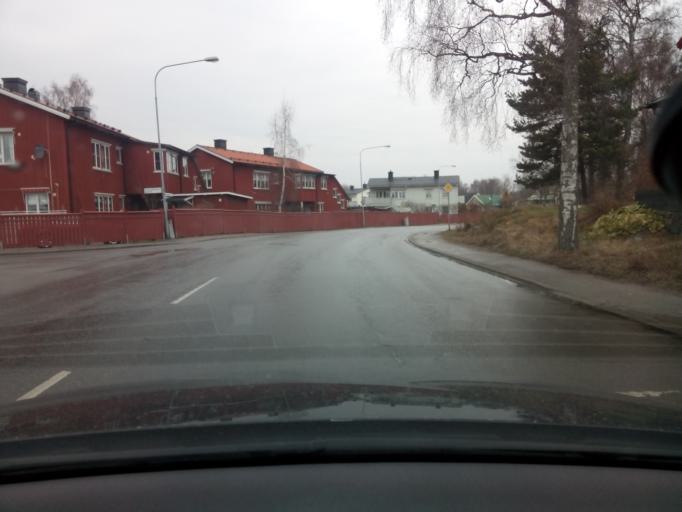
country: SE
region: Soedermanland
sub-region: Trosa Kommun
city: Trosa
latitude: 58.8921
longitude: 17.5533
